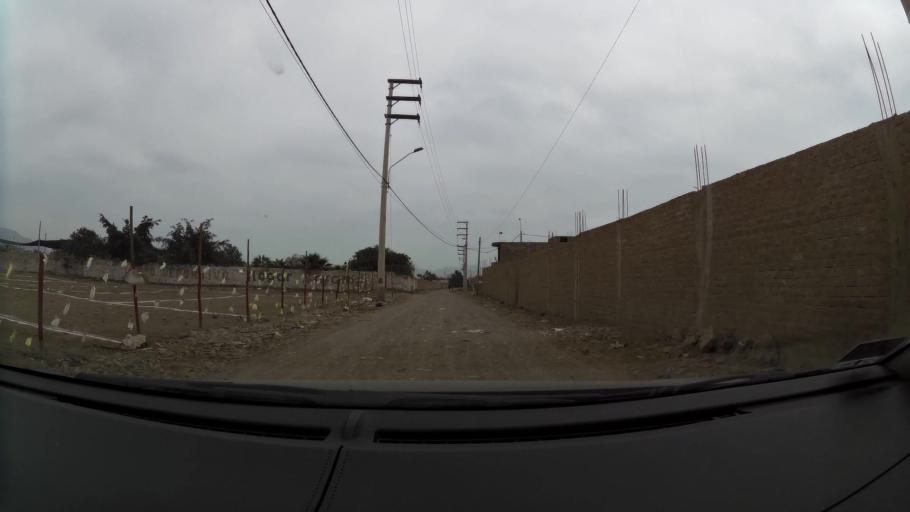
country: PE
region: Lima
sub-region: Provincia de Huaral
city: Huaral
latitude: -11.4858
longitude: -77.2083
